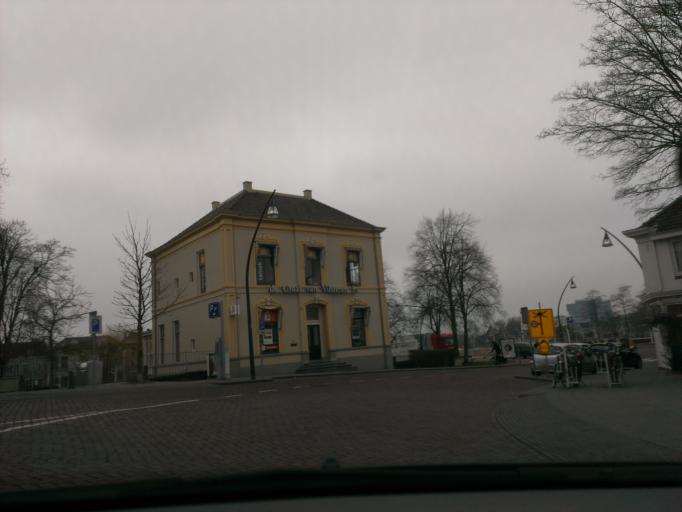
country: NL
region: Overijssel
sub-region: Gemeente Zwolle
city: Zwolle
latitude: 52.5114
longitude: 6.0884
